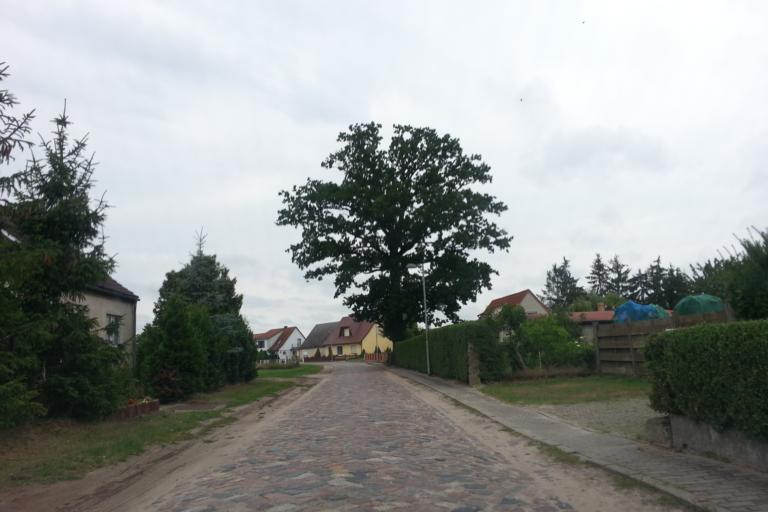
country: DE
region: Mecklenburg-Vorpommern
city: Ferdinandshof
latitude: 53.6958
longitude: 13.8855
